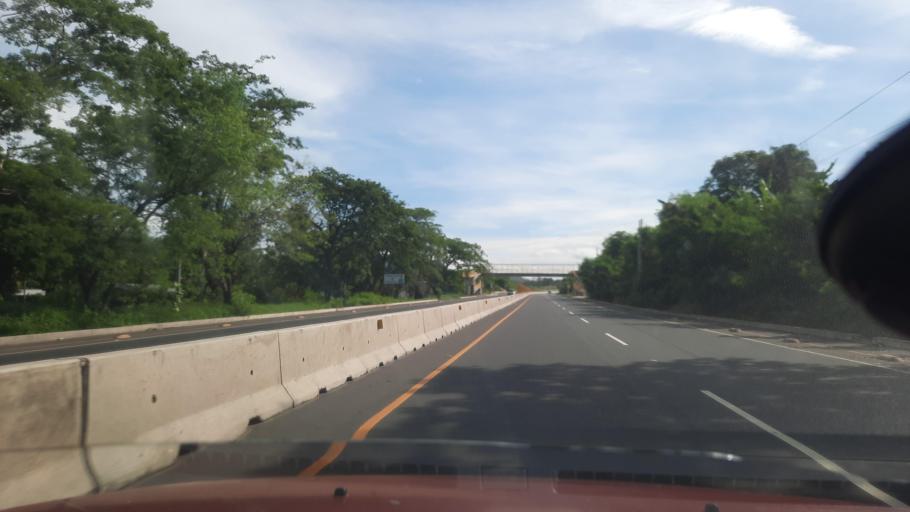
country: SV
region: La Paz
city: El Rosario
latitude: 13.4692
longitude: -89.0041
